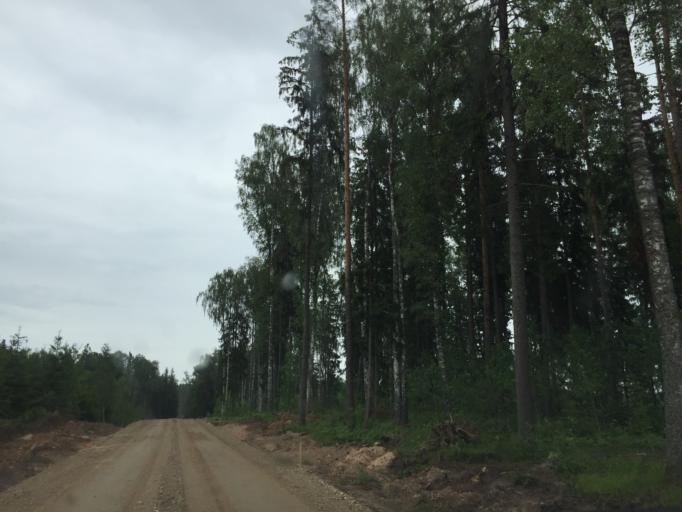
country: LV
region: Tukuma Rajons
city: Tukums
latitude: 57.0052
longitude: 23.1132
